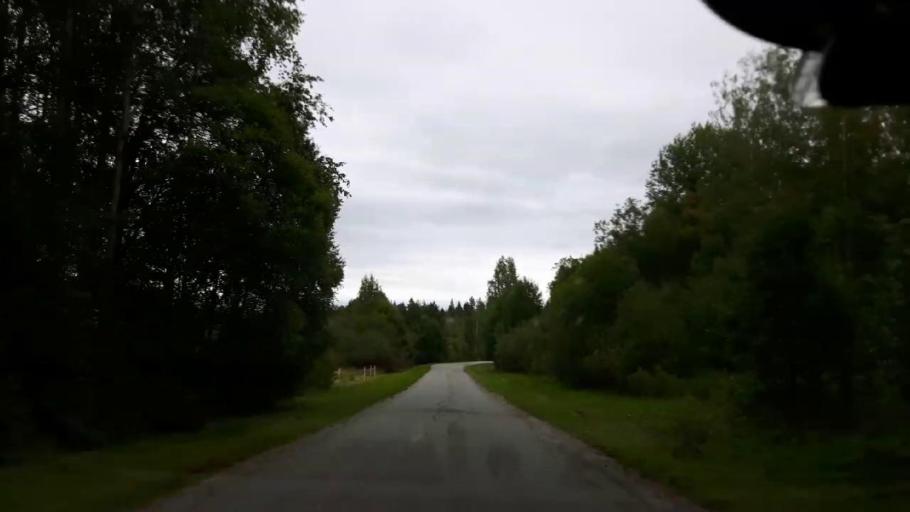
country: SE
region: Vaesternorrland
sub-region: Ange Kommun
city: Fransta
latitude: 62.7720
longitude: 16.0452
